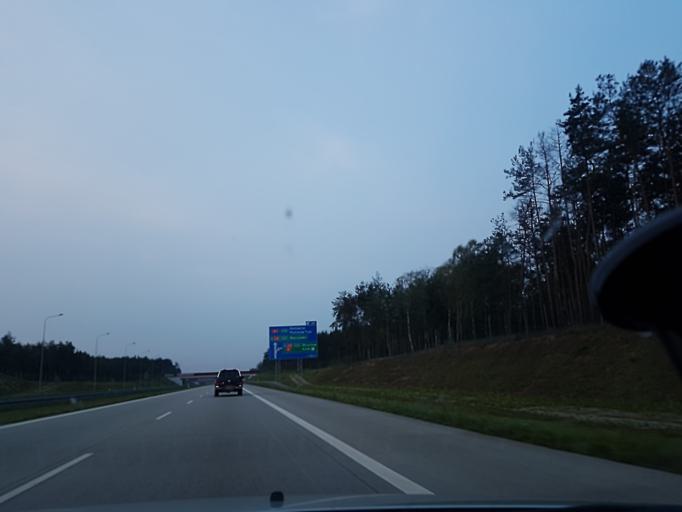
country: PL
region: Lodz Voivodeship
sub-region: Powiat lodzki wschodni
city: Tuszyn
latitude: 51.6554
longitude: 19.5795
